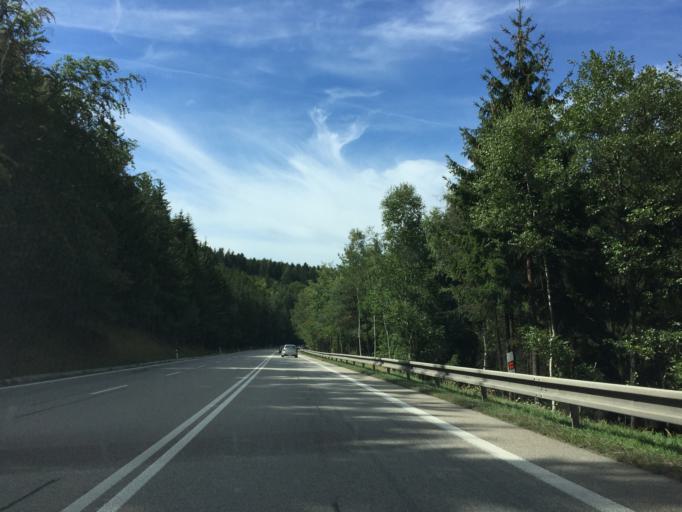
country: CZ
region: Central Bohemia
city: Votice
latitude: 49.6225
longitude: 14.6552
